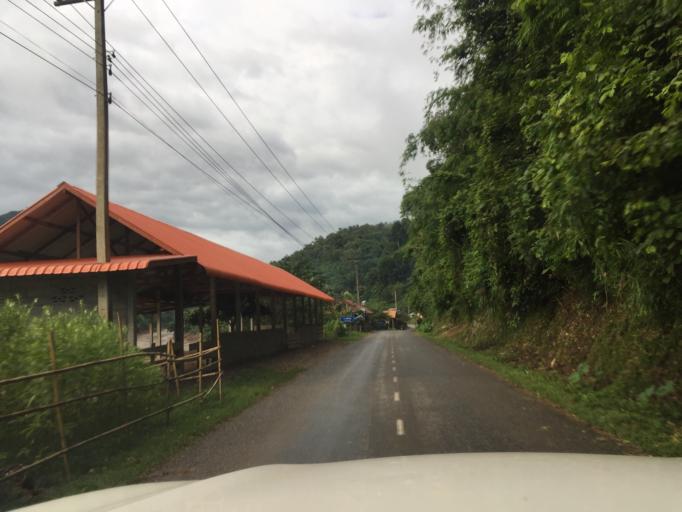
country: LA
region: Oudomxai
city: Muang La
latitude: 21.0573
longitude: 102.2410
